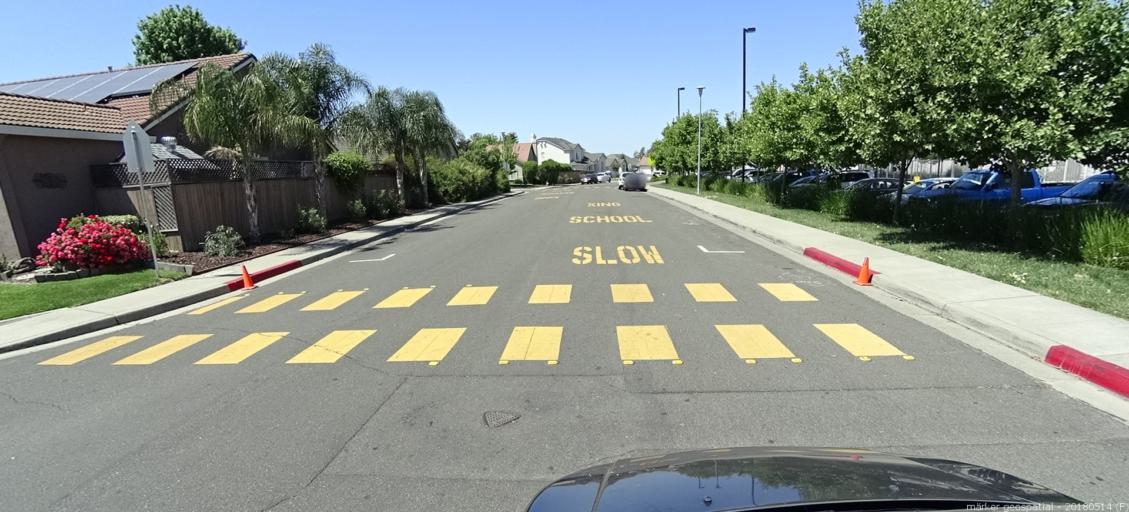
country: US
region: California
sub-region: Yolo County
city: West Sacramento
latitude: 38.6364
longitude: -121.5318
